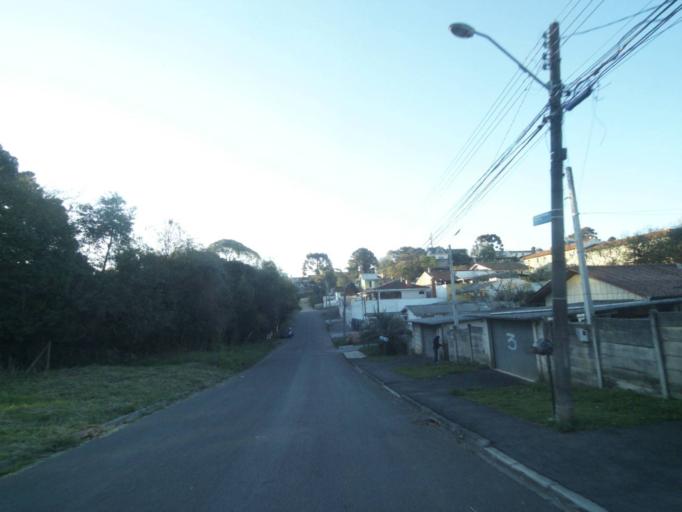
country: BR
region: Parana
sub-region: Curitiba
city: Curitiba
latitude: -25.3872
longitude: -49.2564
